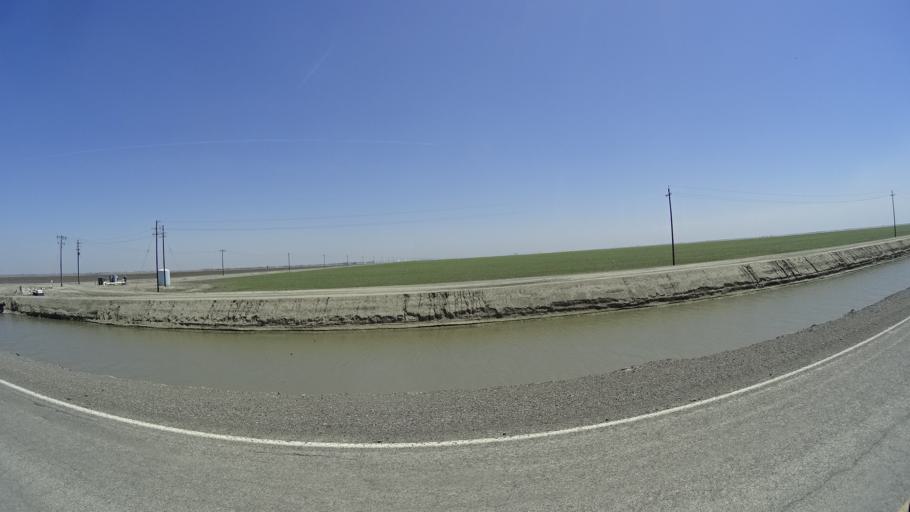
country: US
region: California
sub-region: Kings County
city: Corcoran
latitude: 36.0205
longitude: -119.6433
